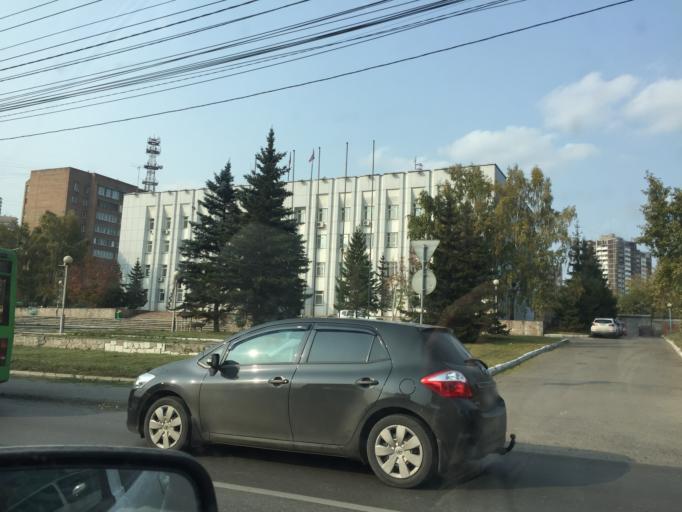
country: RU
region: Krasnoyarskiy
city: Krasnoyarsk
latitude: 56.0332
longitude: 92.9228
